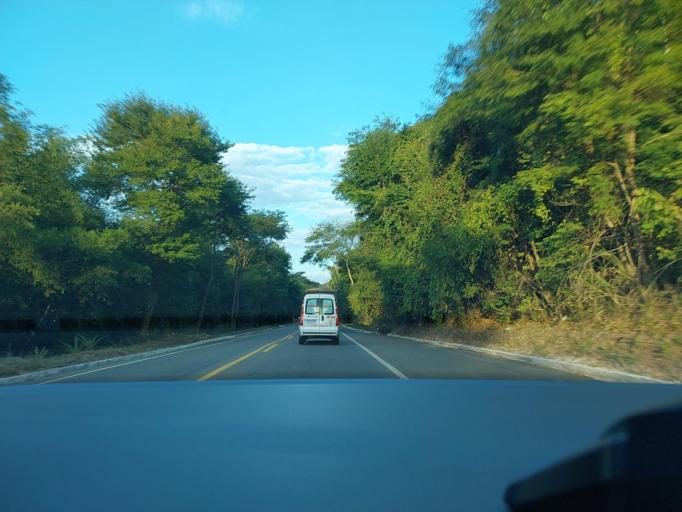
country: BR
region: Minas Gerais
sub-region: Muriae
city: Muriae
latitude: -21.1312
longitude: -42.1948
